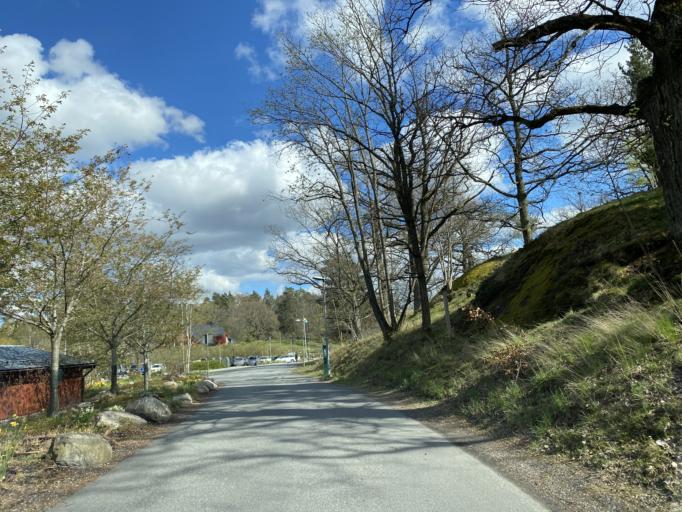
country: SE
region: Stockholm
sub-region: Stockholms Kommun
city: OEstermalm
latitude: 59.3640
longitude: 18.0718
